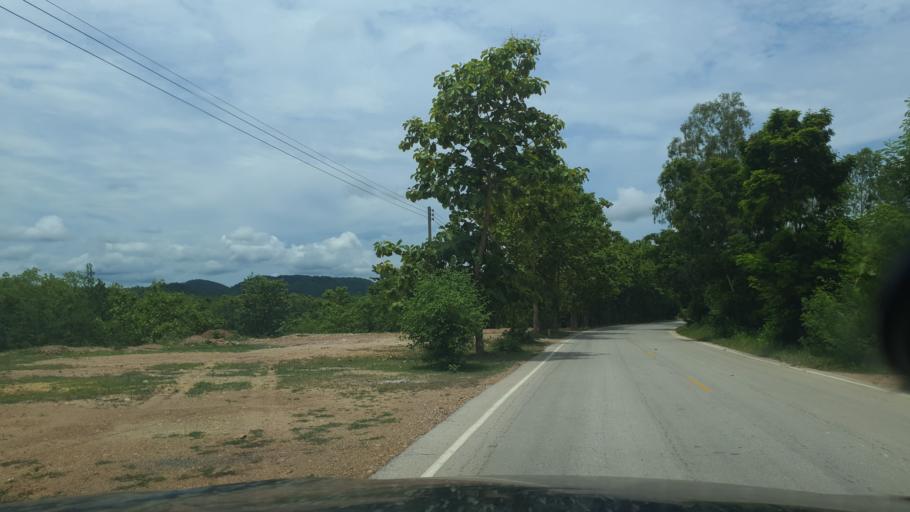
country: TH
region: Lampang
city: Sop Prap
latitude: 17.9194
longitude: 99.4040
